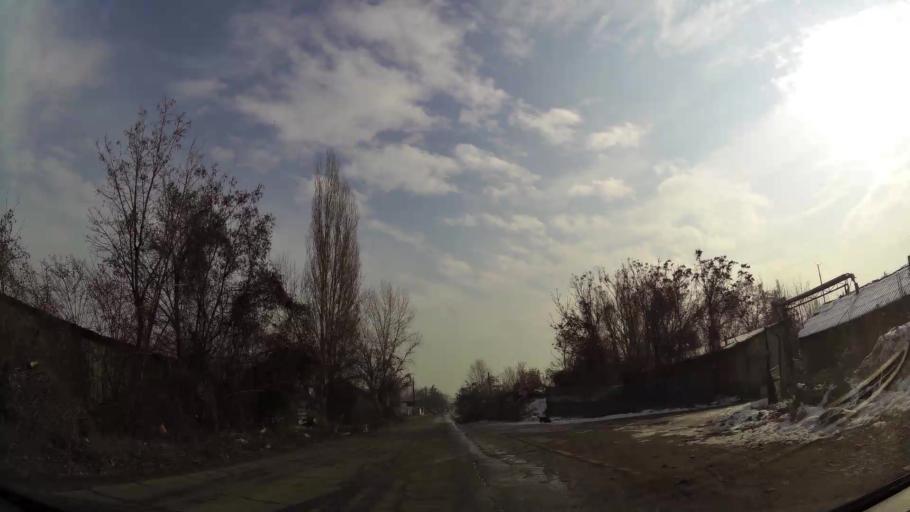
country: MK
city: Krushopek
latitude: 42.0135
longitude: 21.3749
